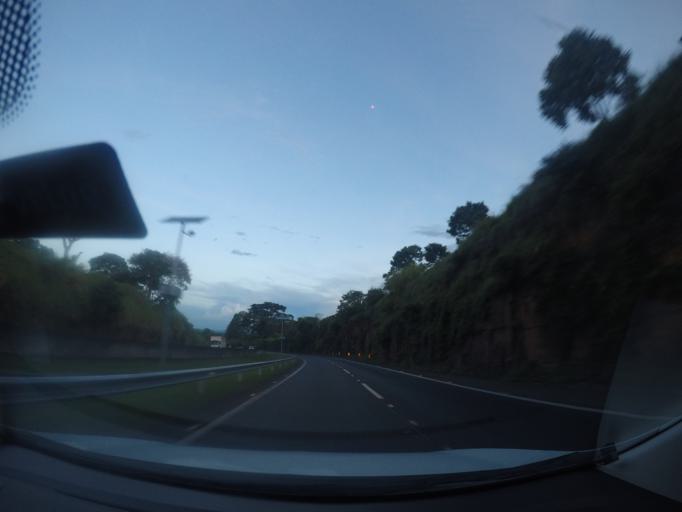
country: BR
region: Sao Paulo
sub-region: Itirapina
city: Itirapina
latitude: -22.2733
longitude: -47.7008
